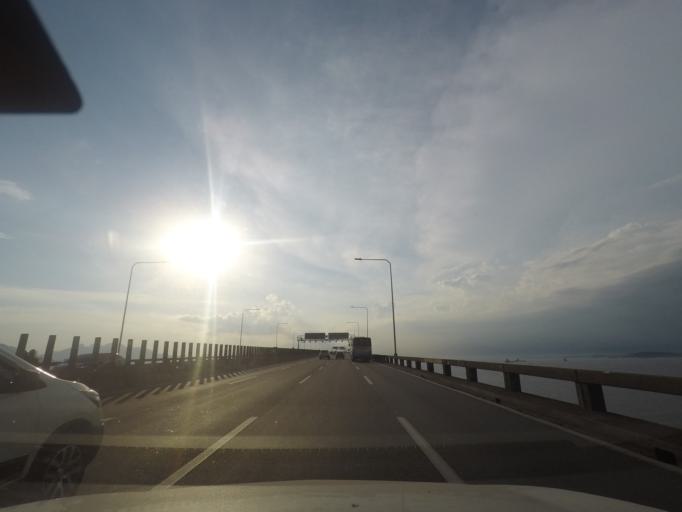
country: BR
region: Rio de Janeiro
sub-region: Niteroi
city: Niteroi
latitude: -22.8725
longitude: -43.1376
